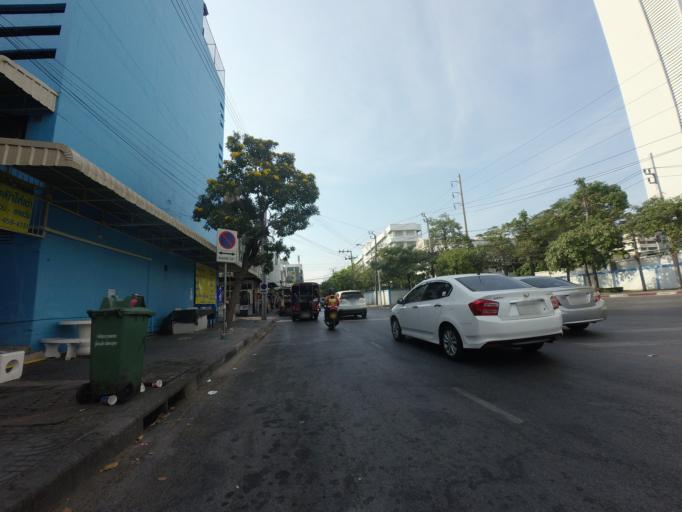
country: TH
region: Bangkok
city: Wang Thonglang
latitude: 13.7540
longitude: 100.6151
